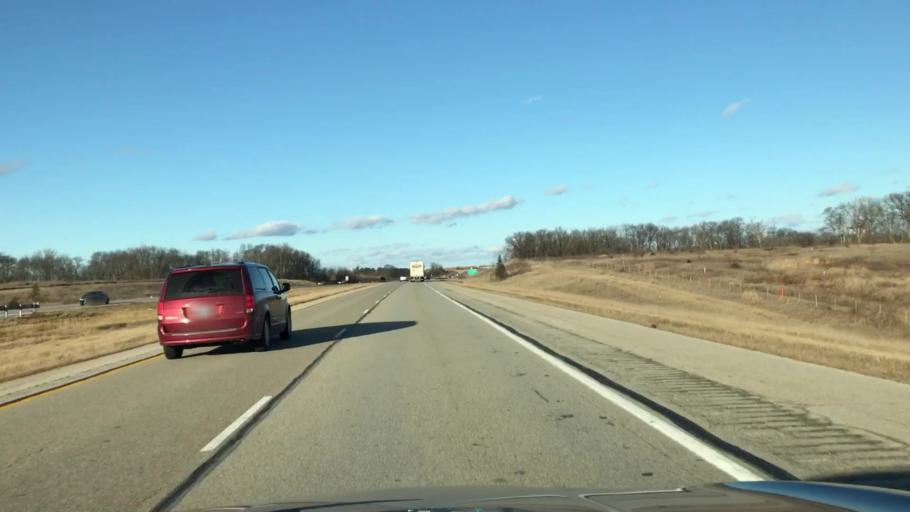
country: US
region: Illinois
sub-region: McLean County
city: Lexington
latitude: 40.6311
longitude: -88.8156
